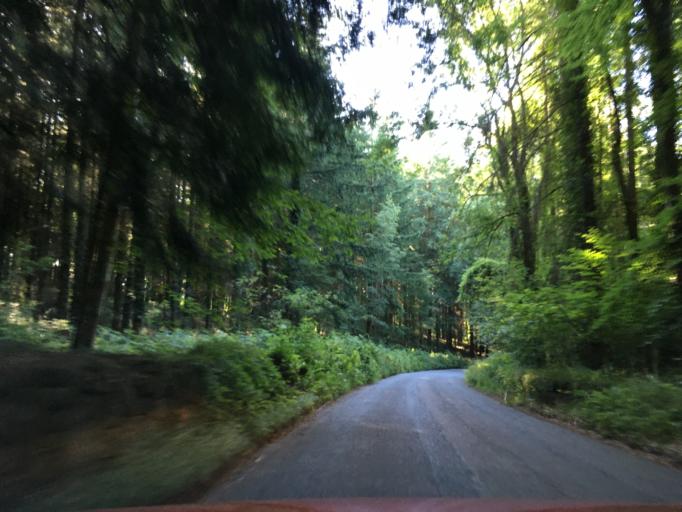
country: GB
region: Wales
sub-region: Monmouthshire
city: Tintern
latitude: 51.7224
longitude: -2.6912
